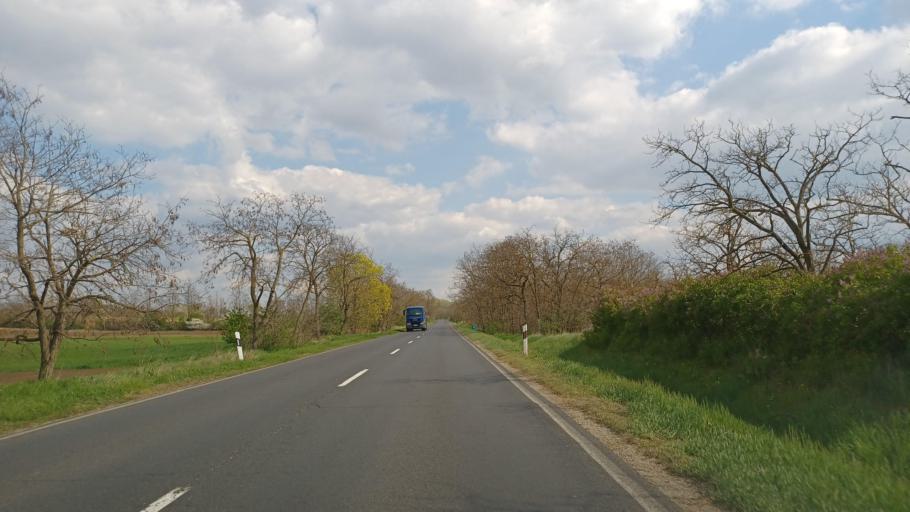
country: HU
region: Fejer
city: Cece
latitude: 46.7428
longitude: 18.6502
